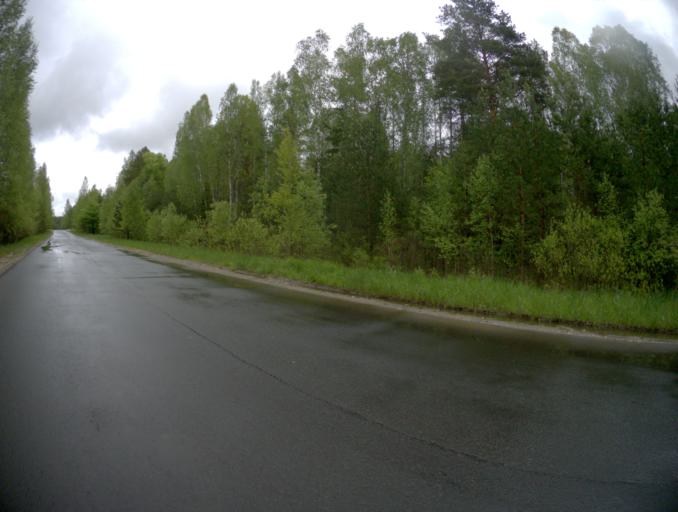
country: RU
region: Vladimir
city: Zolotkovo
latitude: 55.2819
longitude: 41.0437
